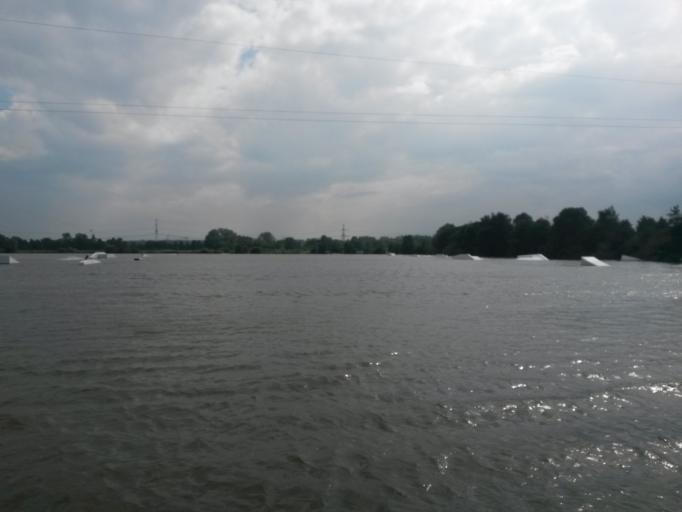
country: DE
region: Hamburg
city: Harburg
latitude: 53.4590
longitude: 10.0154
